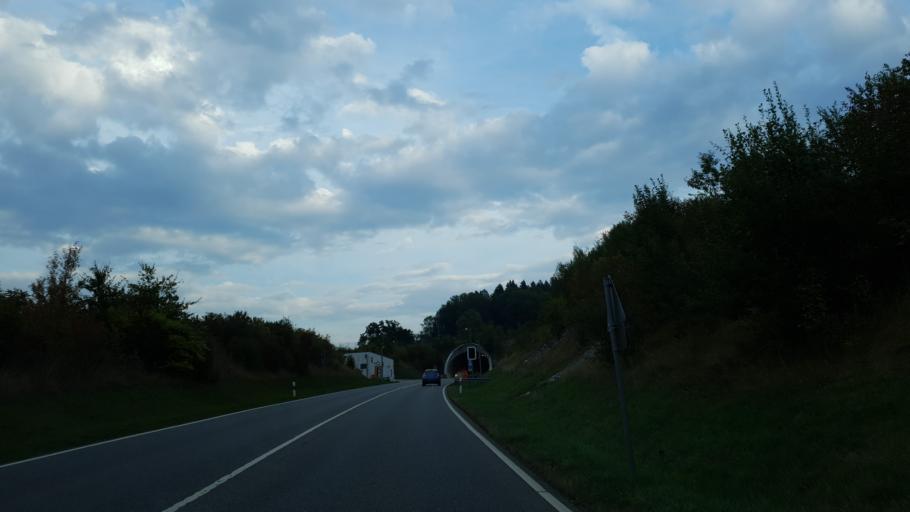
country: DE
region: Baden-Wuerttemberg
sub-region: Tuebingen Region
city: Isny im Allgau
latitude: 47.6852
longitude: 10.0254
